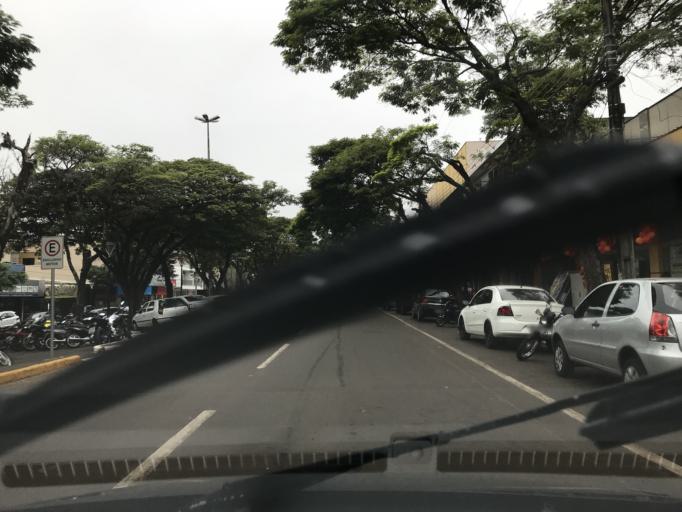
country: PY
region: Canindeyu
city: Salto del Guaira
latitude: -24.0813
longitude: -54.2523
